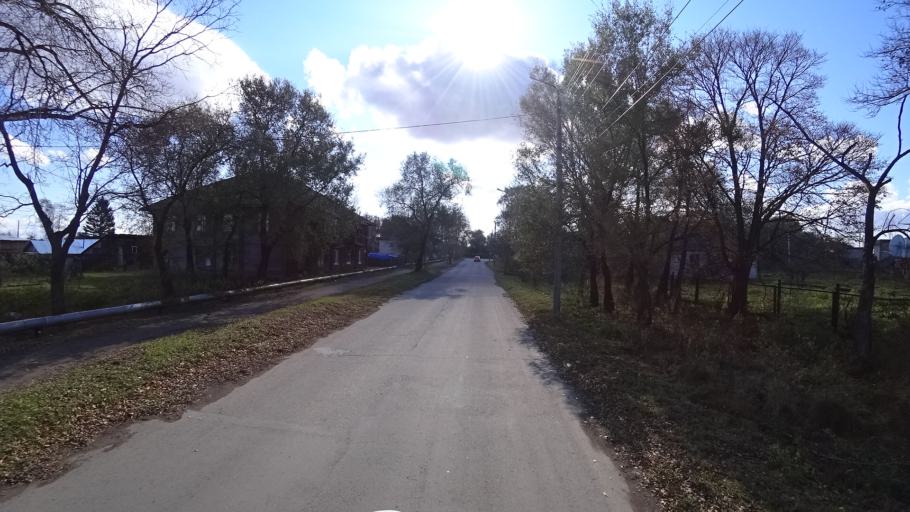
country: RU
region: Khabarovsk Krai
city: Amursk
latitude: 50.0967
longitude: 136.4982
